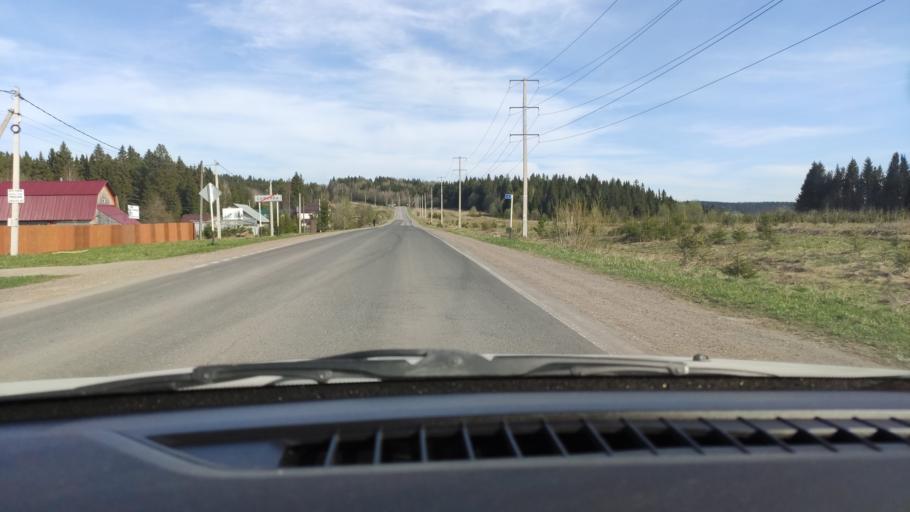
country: RU
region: Perm
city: Novyye Lyady
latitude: 57.9343
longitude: 56.6339
